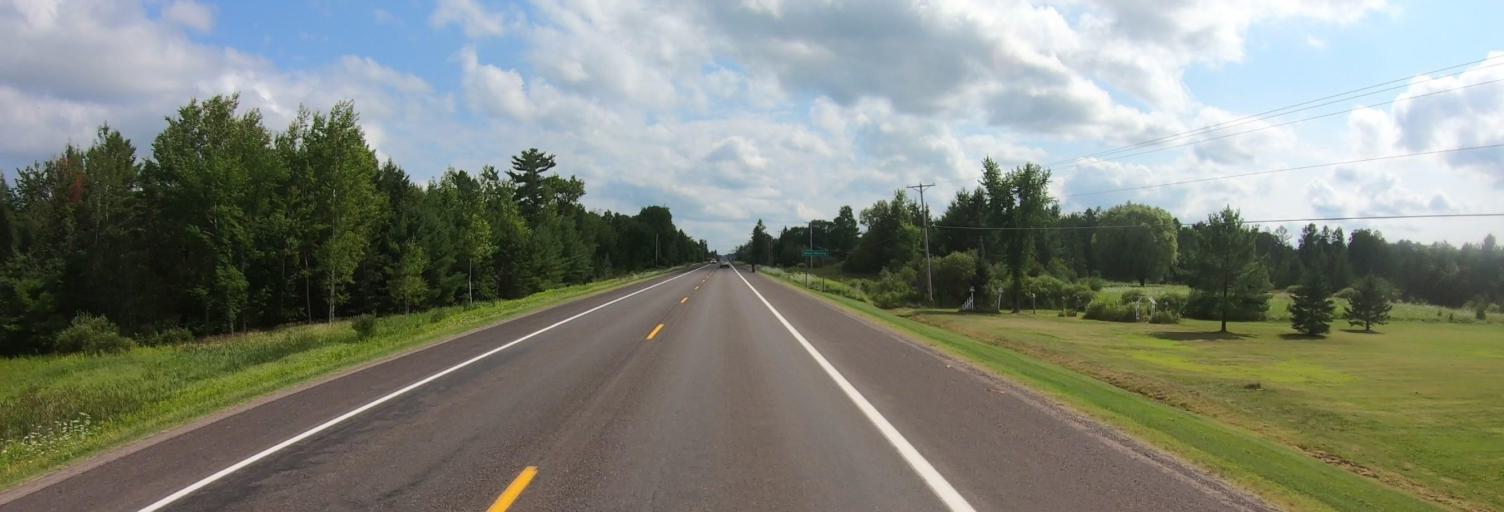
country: US
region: Michigan
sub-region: Ontonagon County
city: Ontonagon
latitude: 46.5440
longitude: -89.1786
